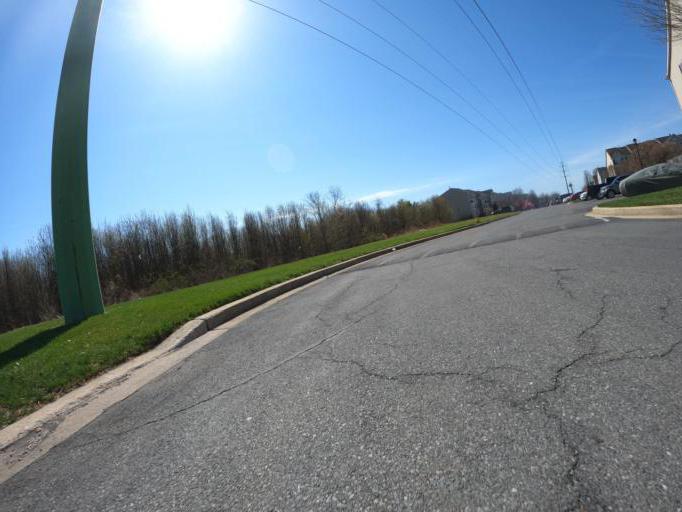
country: US
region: Maryland
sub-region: Frederick County
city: Ballenger Creek
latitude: 39.3772
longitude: -77.4250
